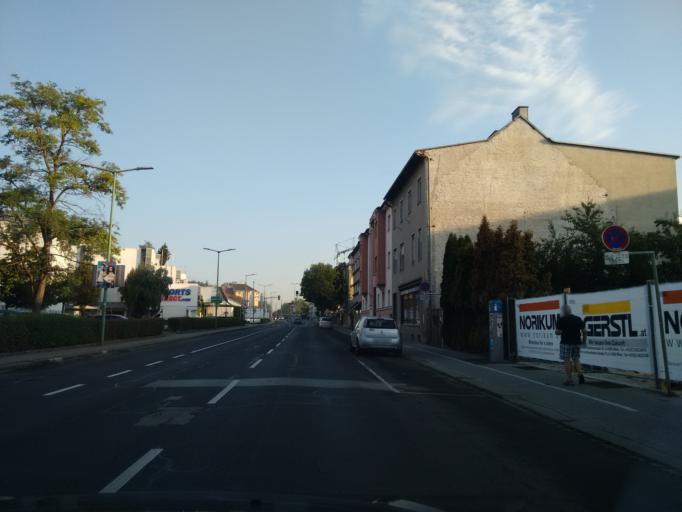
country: AT
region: Upper Austria
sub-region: Wels Stadt
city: Wels
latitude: 48.1614
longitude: 14.0268
